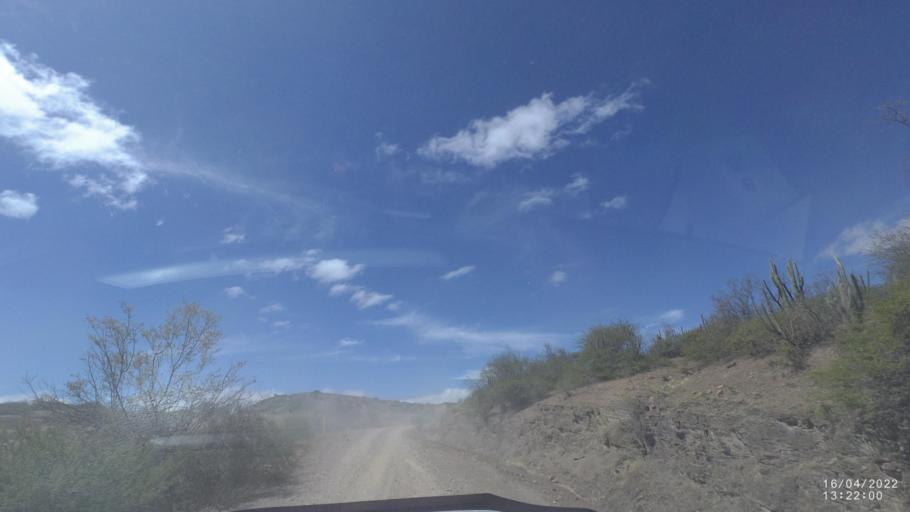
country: BO
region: Cochabamba
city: Mizque
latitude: -17.9922
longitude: -65.6085
